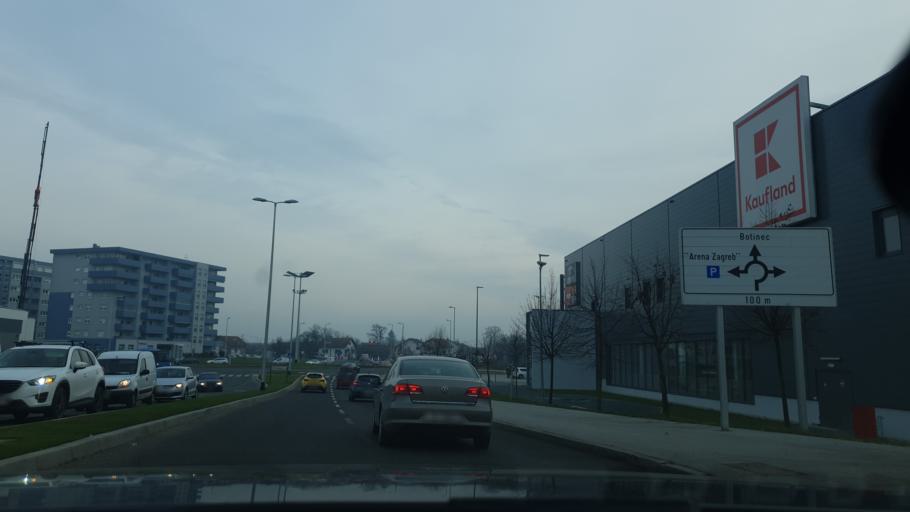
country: HR
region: Grad Zagreb
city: Zadvorsko
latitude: 45.7697
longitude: 15.9339
